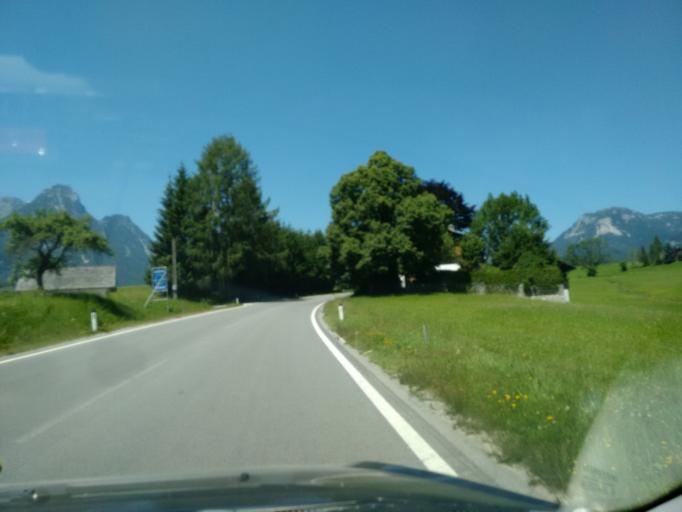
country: AT
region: Styria
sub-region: Politischer Bezirk Liezen
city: Bad Aussee
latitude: 47.6113
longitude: 13.7696
